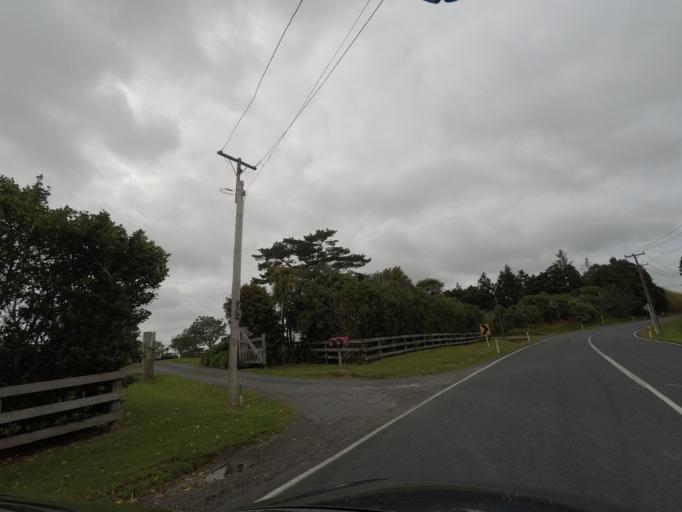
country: NZ
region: Auckland
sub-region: Auckland
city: Rosebank
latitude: -36.8230
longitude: 174.5780
